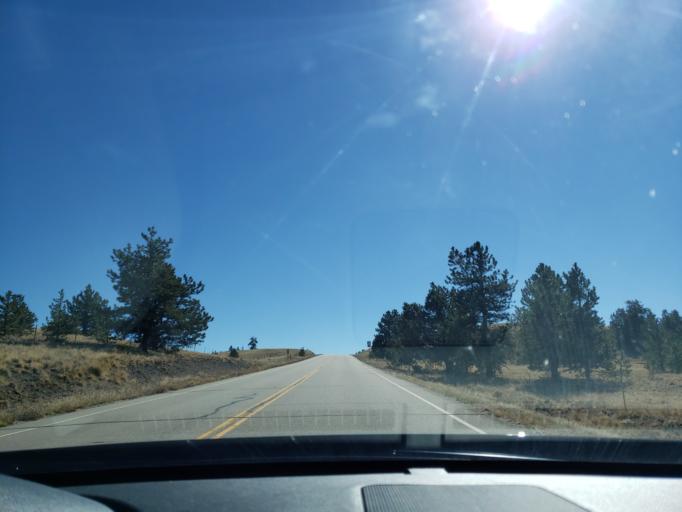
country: US
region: Colorado
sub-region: Chaffee County
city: Buena Vista
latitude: 38.8935
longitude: -105.6891
